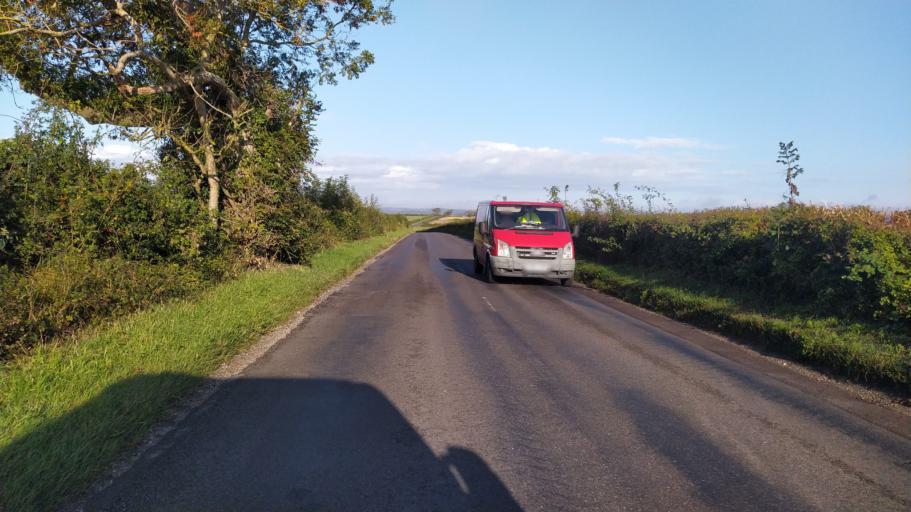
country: GB
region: England
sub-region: Wiltshire
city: Bower Chalke
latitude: 50.8988
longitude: -2.0233
